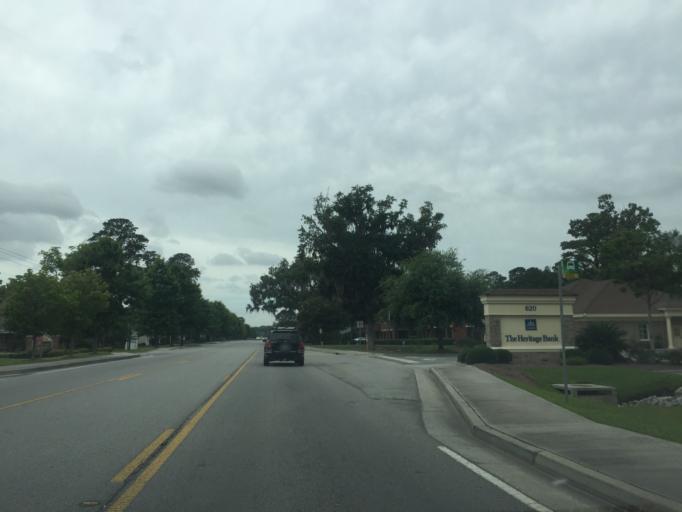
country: US
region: Georgia
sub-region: Chatham County
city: Isle of Hope
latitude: 32.0106
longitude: -81.1018
